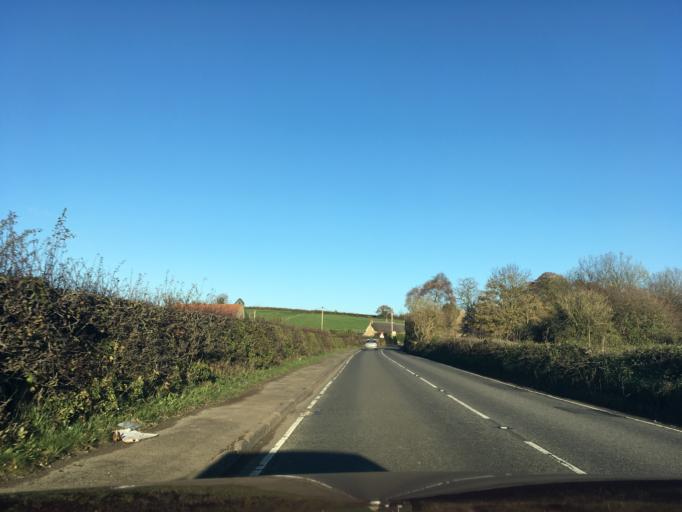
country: GB
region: England
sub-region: Dorset
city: Sherborne
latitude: 50.9583
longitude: -2.4964
